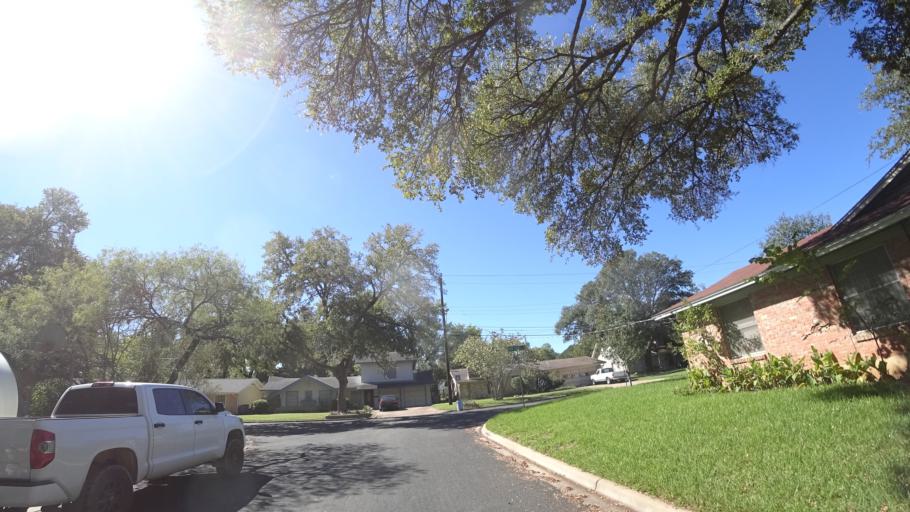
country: US
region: Texas
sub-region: Travis County
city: Rollingwood
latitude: 30.2215
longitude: -97.7986
